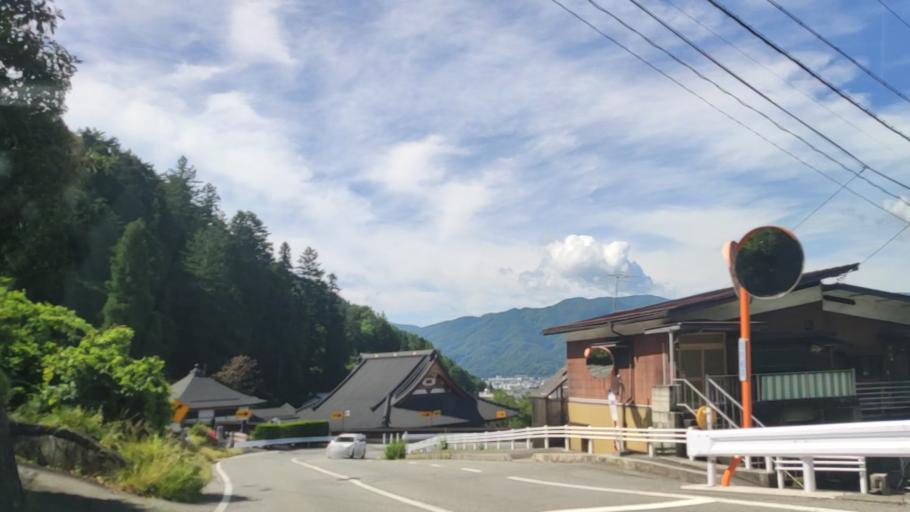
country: JP
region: Nagano
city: Suwa
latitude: 36.0440
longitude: 138.1267
